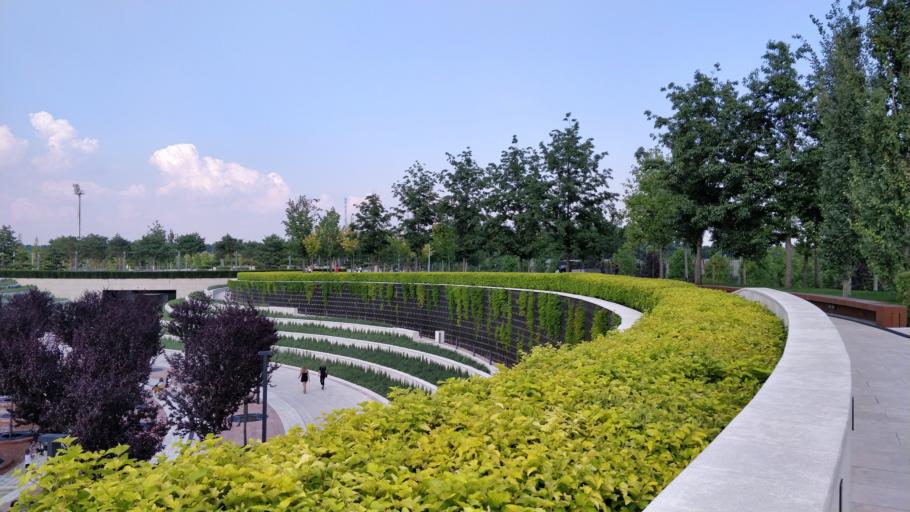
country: RU
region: Krasnodarskiy
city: Krasnodar
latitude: 45.0408
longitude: 39.0335
